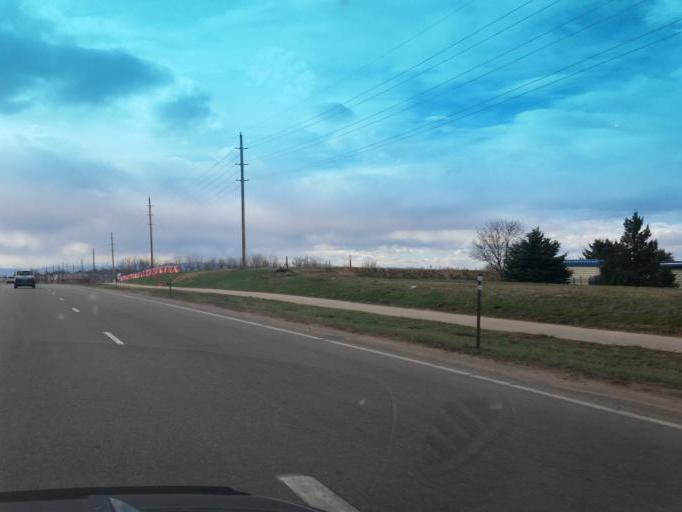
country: US
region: Colorado
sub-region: Weld County
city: Greeley
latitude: 40.3924
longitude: -104.7372
